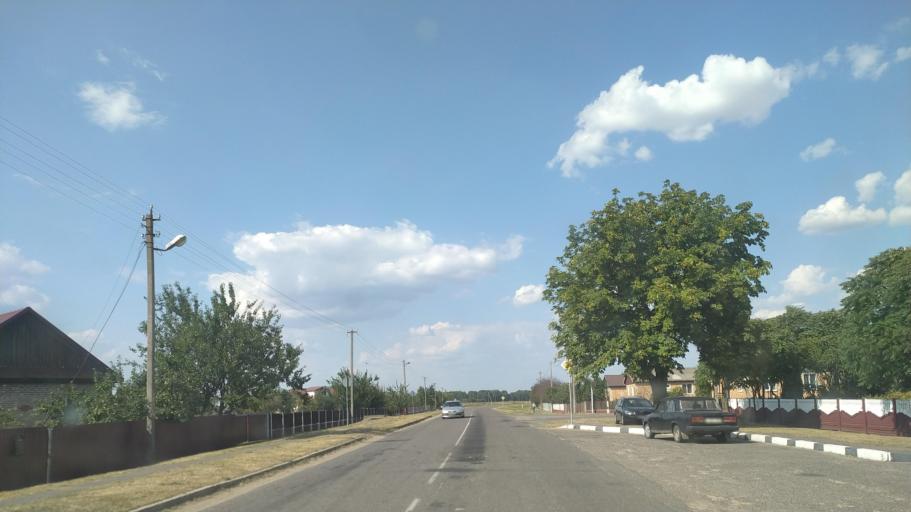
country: BY
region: Brest
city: Drahichyn
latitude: 52.1205
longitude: 25.1169
